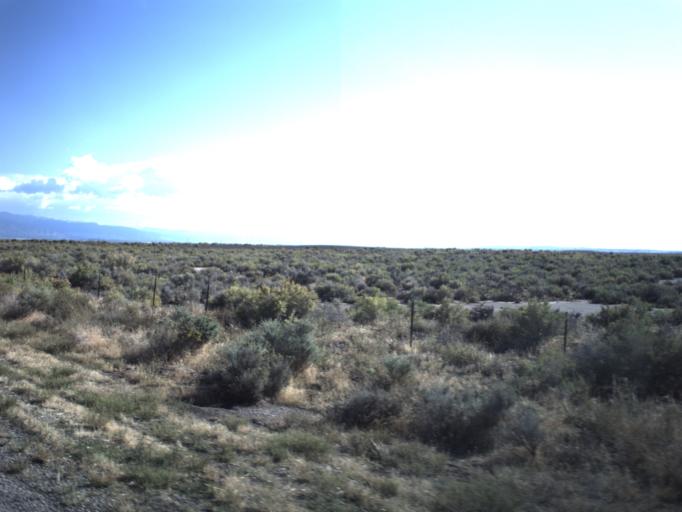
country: US
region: Utah
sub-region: Millard County
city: Delta
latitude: 39.2642
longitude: -112.4497
